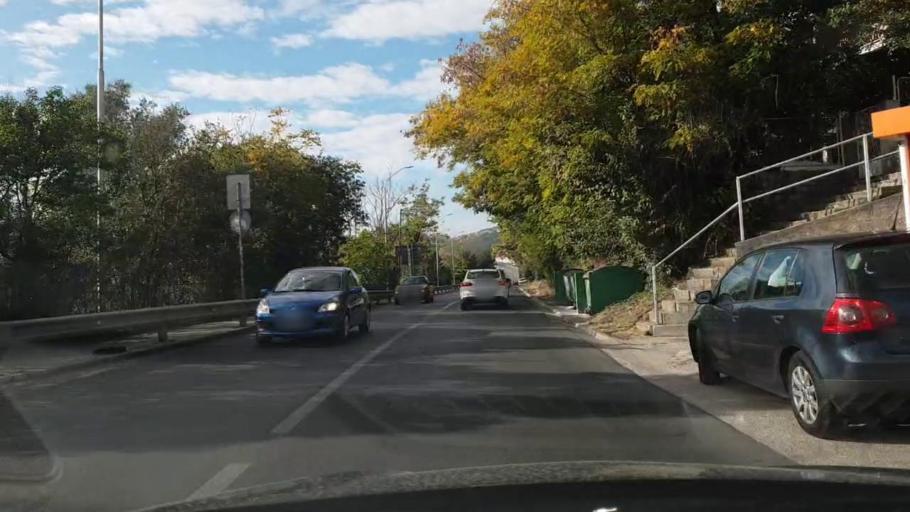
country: ME
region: Herceg Novi
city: Herceg-Novi
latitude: 42.4533
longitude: 18.5334
